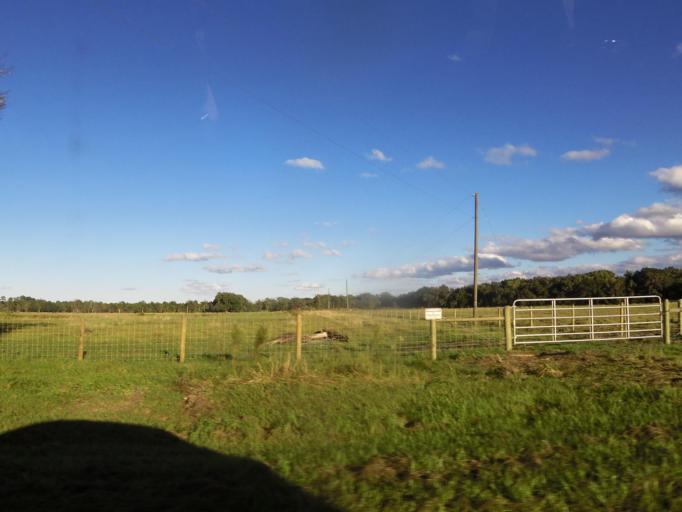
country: US
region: Florida
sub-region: Marion County
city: Citra
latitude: 29.4602
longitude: -82.1056
